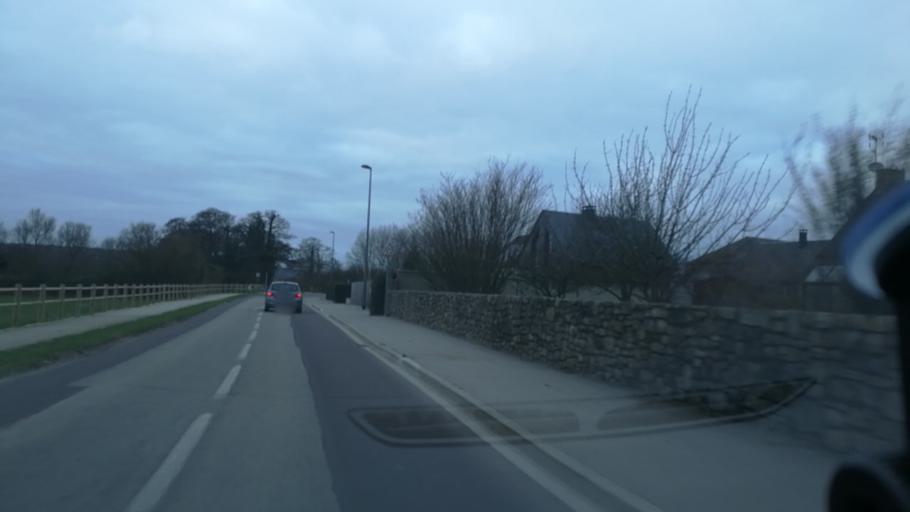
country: FR
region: Lower Normandy
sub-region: Departement de la Manche
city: Reville
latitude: 49.6150
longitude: -1.2592
